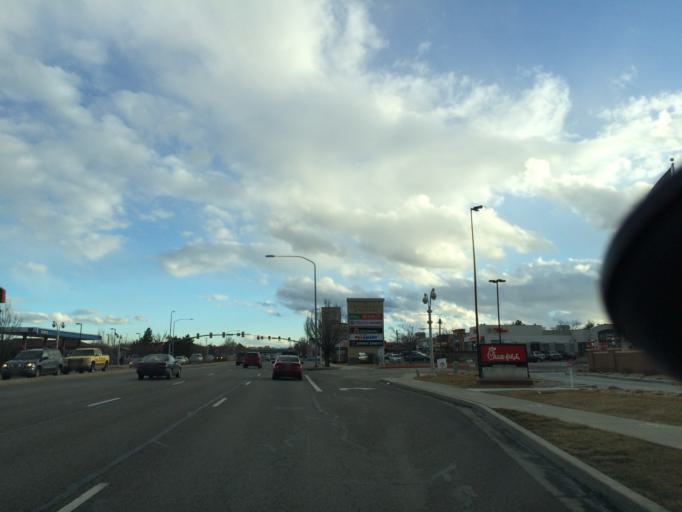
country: US
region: Utah
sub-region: Salt Lake County
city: Taylorsville
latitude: 40.6509
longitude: -111.9389
